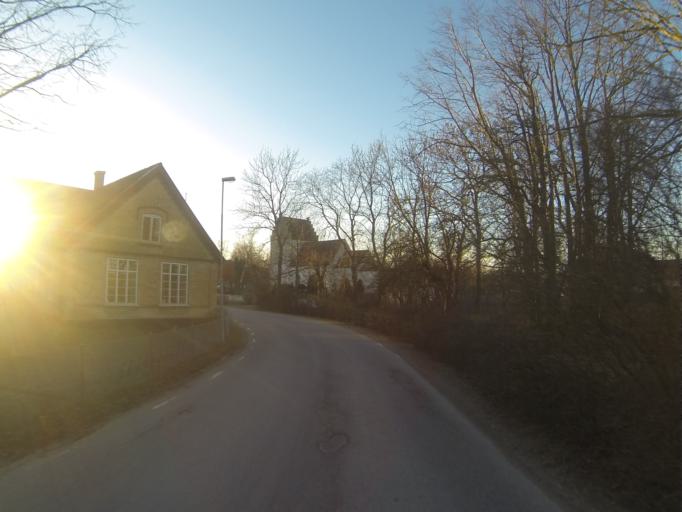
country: SE
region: Skane
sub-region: Staffanstorps Kommun
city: Staffanstorp
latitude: 55.6079
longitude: 13.1782
